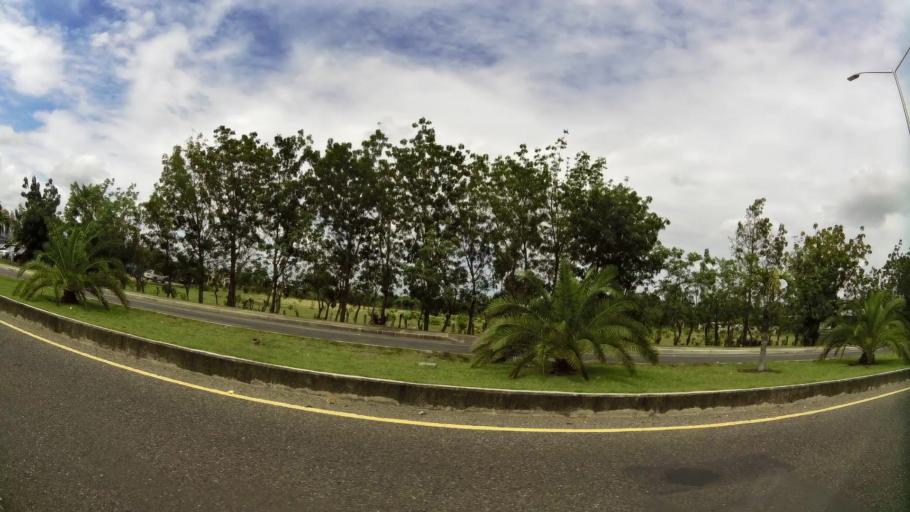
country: DO
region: Santiago
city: Licey al Medio
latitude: 19.3982
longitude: -70.6030
